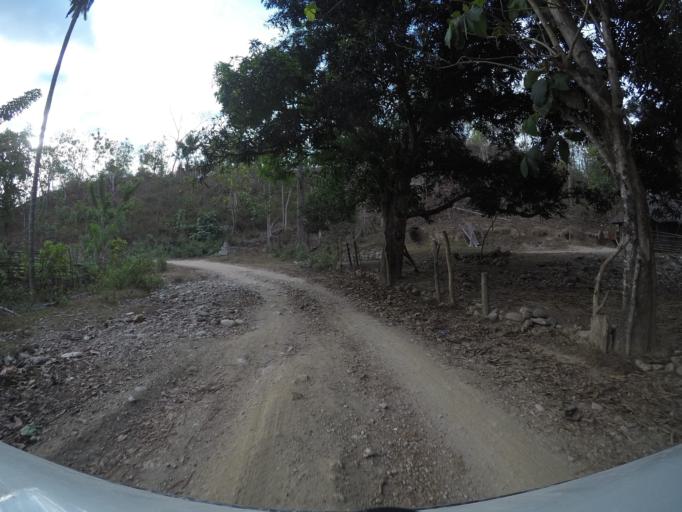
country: TL
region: Bobonaro
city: Maliana
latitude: -8.8904
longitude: 125.2100
